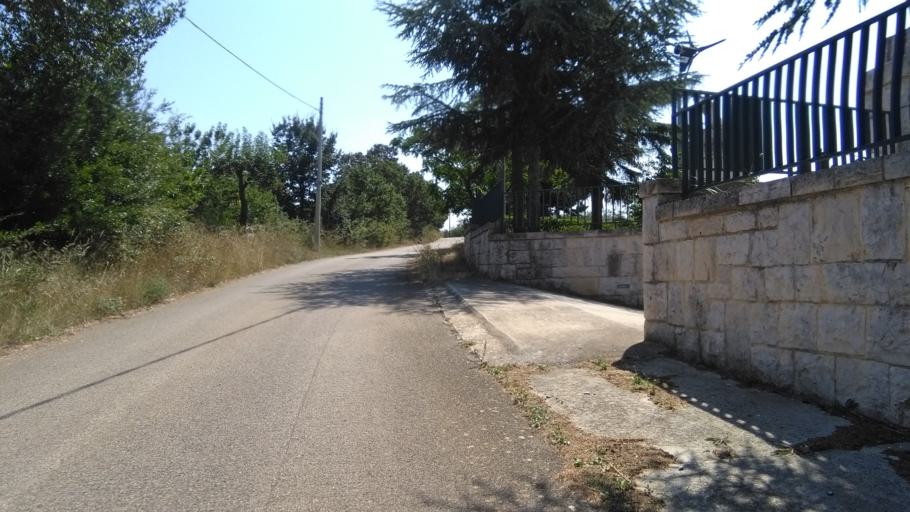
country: IT
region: Apulia
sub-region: Provincia di Bari
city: Noci
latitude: 40.8165
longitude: 17.1594
